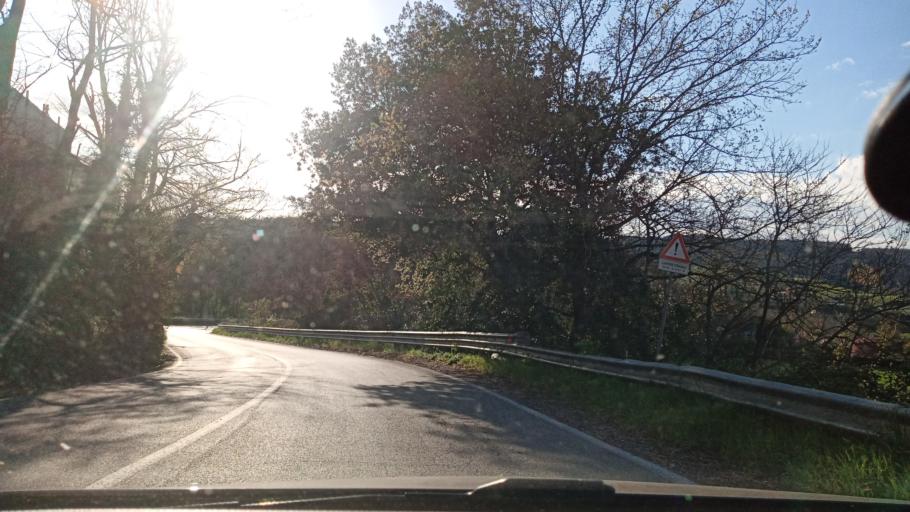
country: IT
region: Latium
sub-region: Citta metropolitana di Roma Capitale
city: Fiano Romano
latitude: 42.1791
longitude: 12.6093
